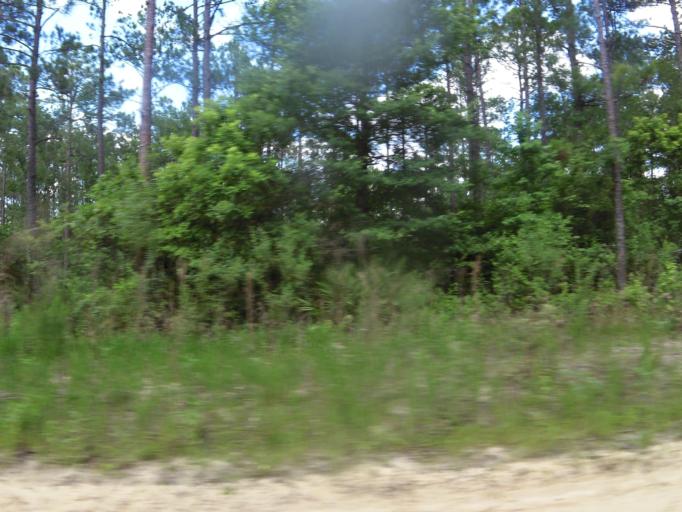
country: US
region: Florida
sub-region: Clay County
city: Asbury Lake
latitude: 29.8923
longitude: -81.8753
